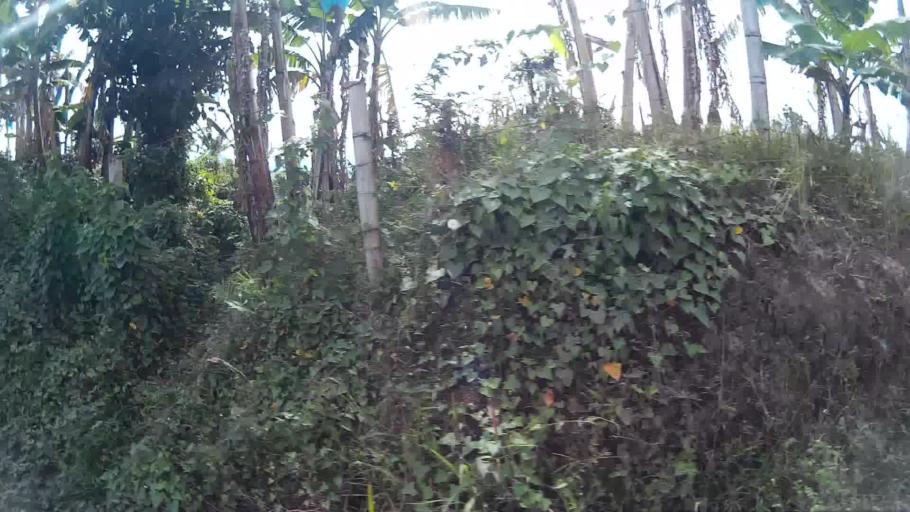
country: CO
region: Caldas
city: Belalcazar
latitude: 4.9652
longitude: -75.8272
